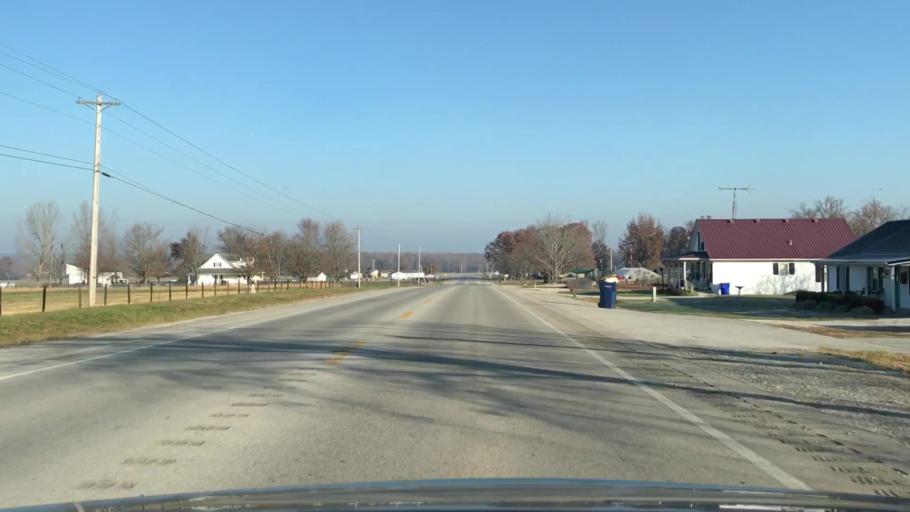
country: US
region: Kentucky
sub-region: Edmonson County
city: Brownsville
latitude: 37.1093
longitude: -86.2293
